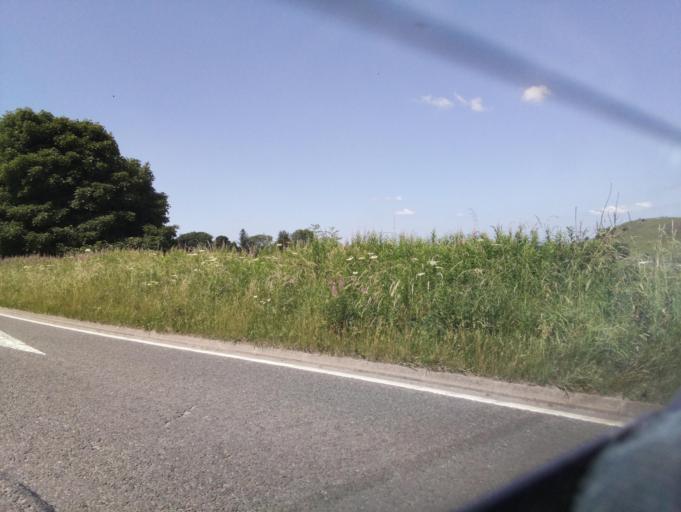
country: GB
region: England
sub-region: Derbyshire
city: Tideswell
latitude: 53.2386
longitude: -1.7958
